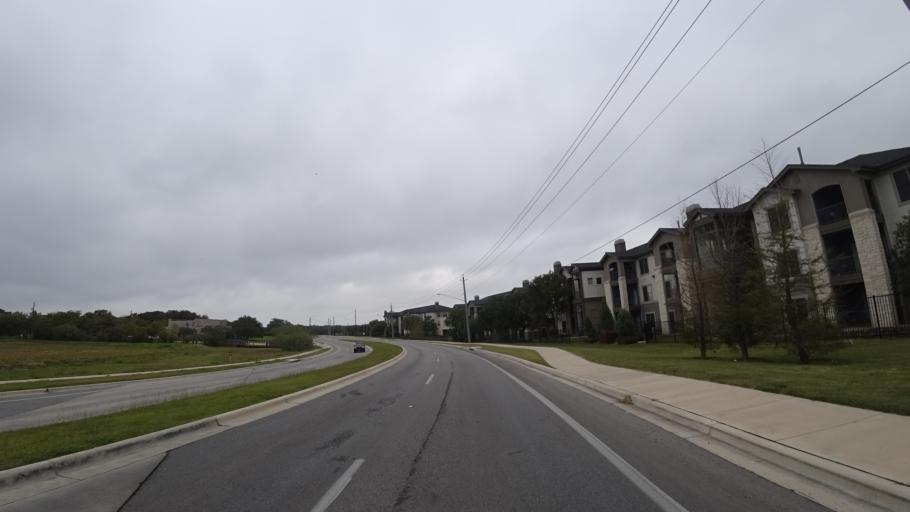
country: US
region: Texas
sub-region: Travis County
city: Shady Hollow
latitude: 30.1961
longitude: -97.8437
